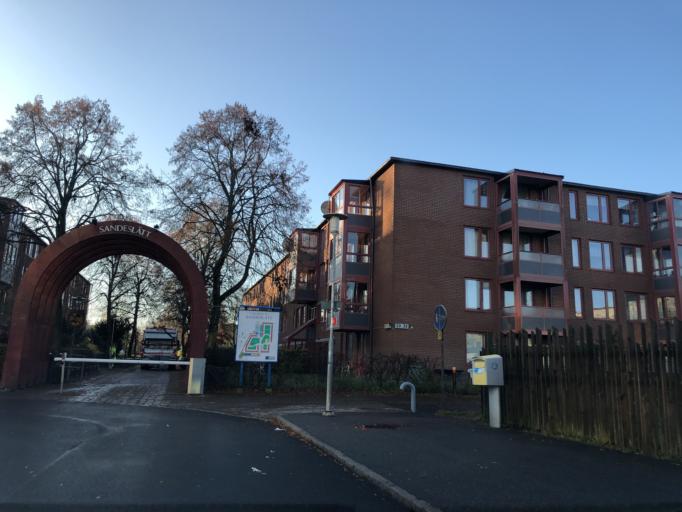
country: SE
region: Vaestra Goetaland
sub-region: Goteborg
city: Hammarkullen
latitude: 57.7782
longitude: 12.0348
